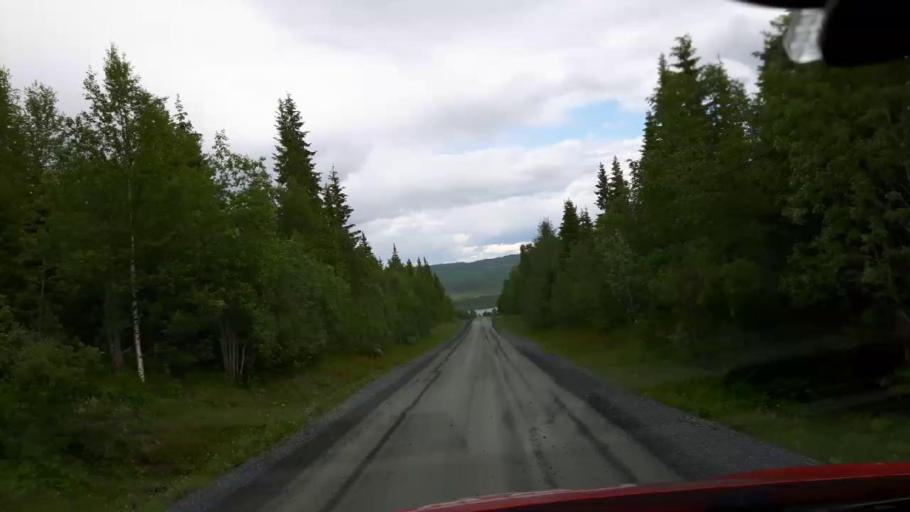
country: NO
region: Nord-Trondelag
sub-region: Lierne
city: Sandvika
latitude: 64.1549
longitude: 13.9992
